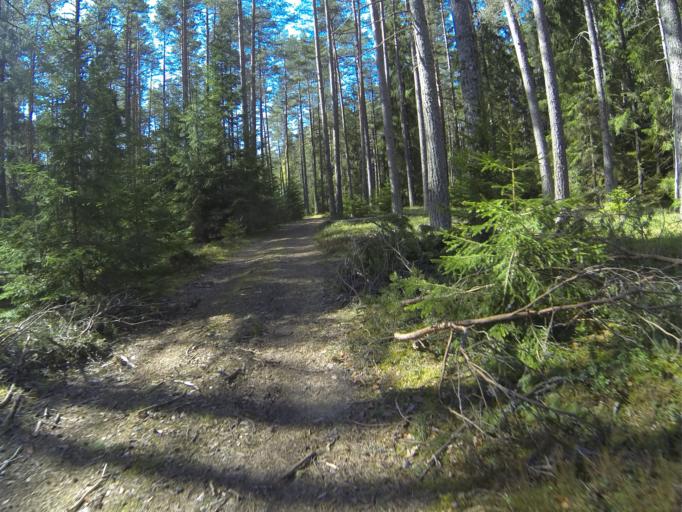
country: FI
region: Varsinais-Suomi
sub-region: Salo
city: Pertteli
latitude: 60.3968
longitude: 23.2129
